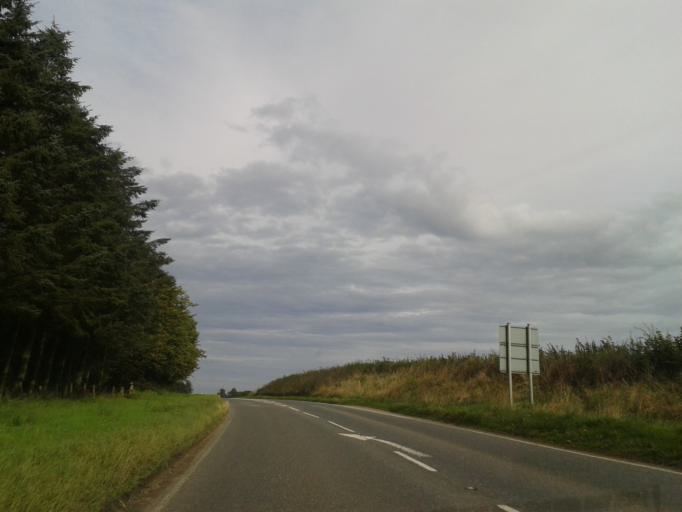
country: GB
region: Scotland
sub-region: Aberdeenshire
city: Rosehearty
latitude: 57.6016
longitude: -2.2219
